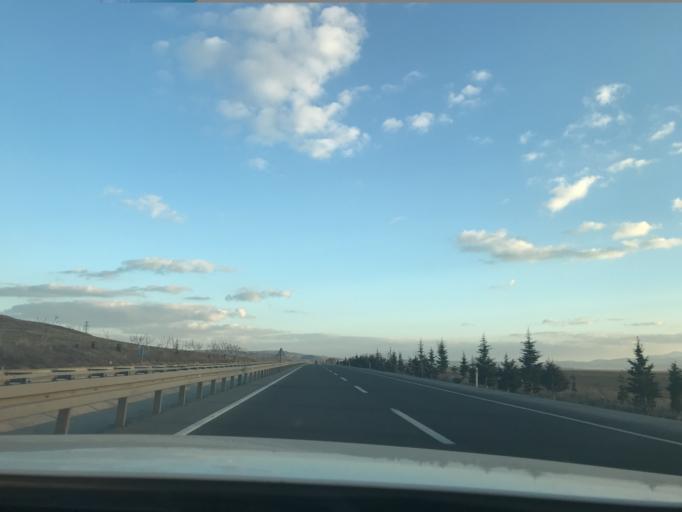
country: TR
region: Ankara
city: Yenice
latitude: 39.4046
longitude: 32.8729
